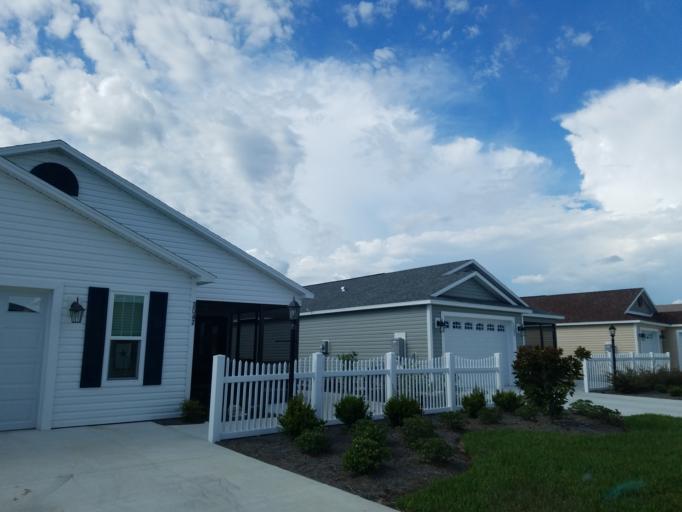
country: US
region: Florida
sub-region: Sumter County
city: Wildwood
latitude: 28.7956
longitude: -82.0318
